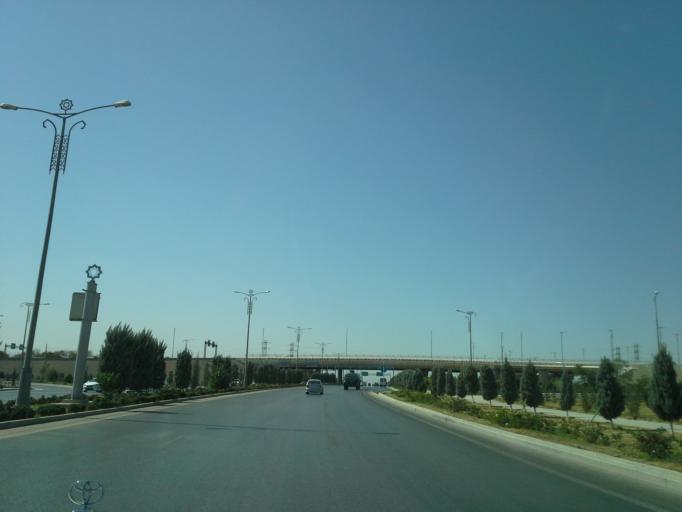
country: TM
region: Ahal
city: Annau
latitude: 37.9121
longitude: 58.4881
